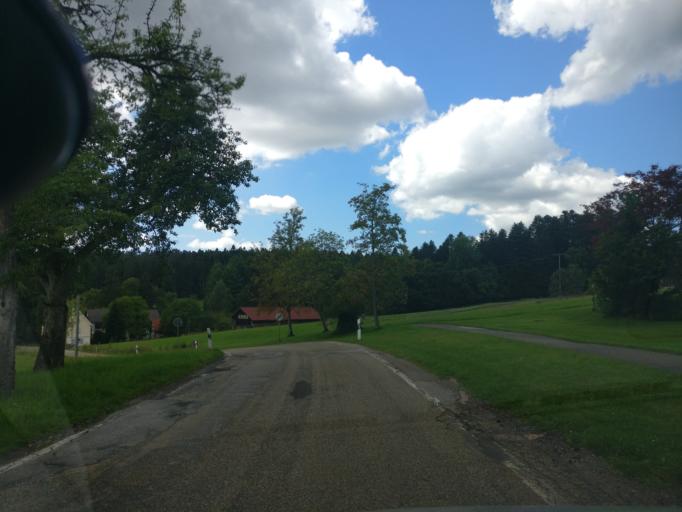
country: DE
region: Baden-Wuerttemberg
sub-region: Karlsruhe Region
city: Lossburg
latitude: 48.4146
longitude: 8.4106
